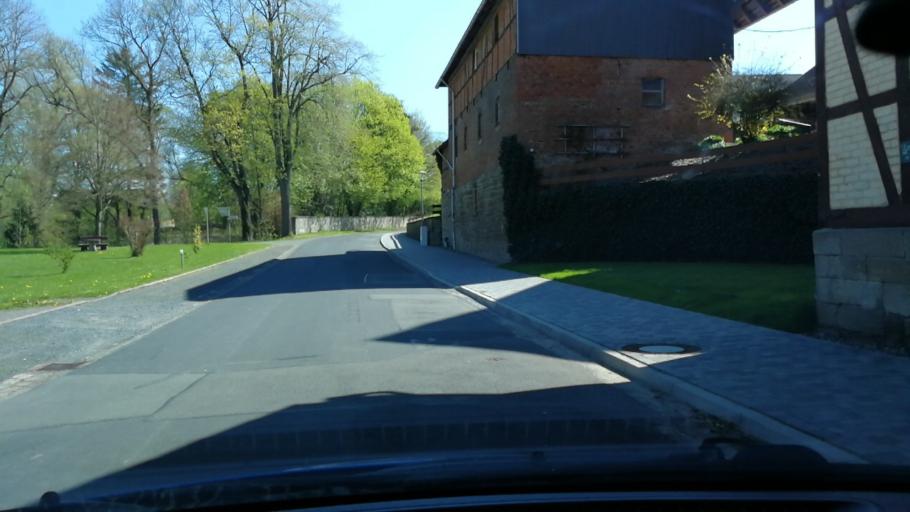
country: DE
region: Lower Saxony
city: Buhren
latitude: 51.5201
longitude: 9.7026
